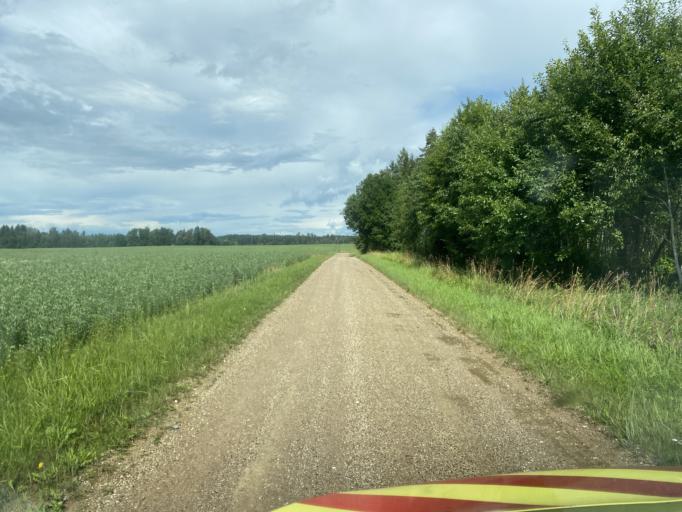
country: EE
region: Valgamaa
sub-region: Torva linn
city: Torva
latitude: 58.1021
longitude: 26.0029
